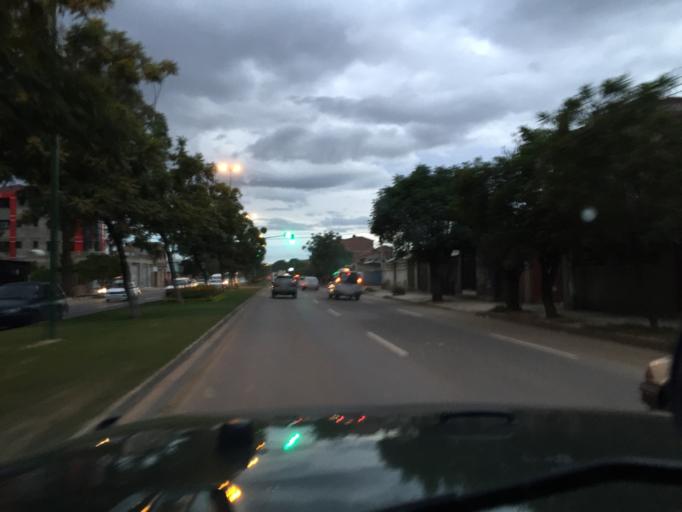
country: BO
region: Cochabamba
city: Cochabamba
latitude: -17.4025
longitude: -66.1819
